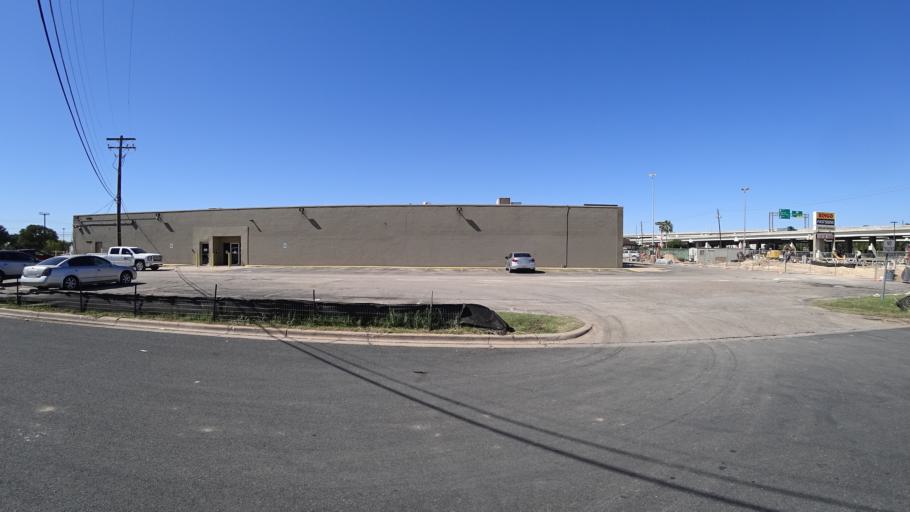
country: US
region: Texas
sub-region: Travis County
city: Rollingwood
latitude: 30.2296
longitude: -97.7905
